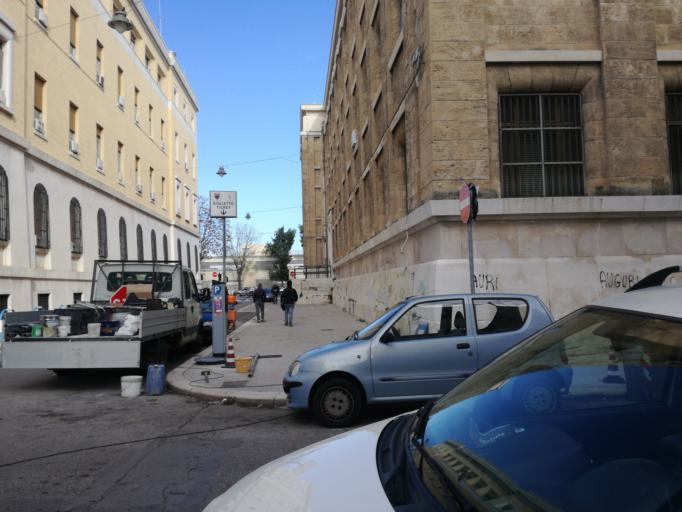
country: IT
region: Apulia
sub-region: Provincia di Bari
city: Bari
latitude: 41.1275
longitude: 16.8596
